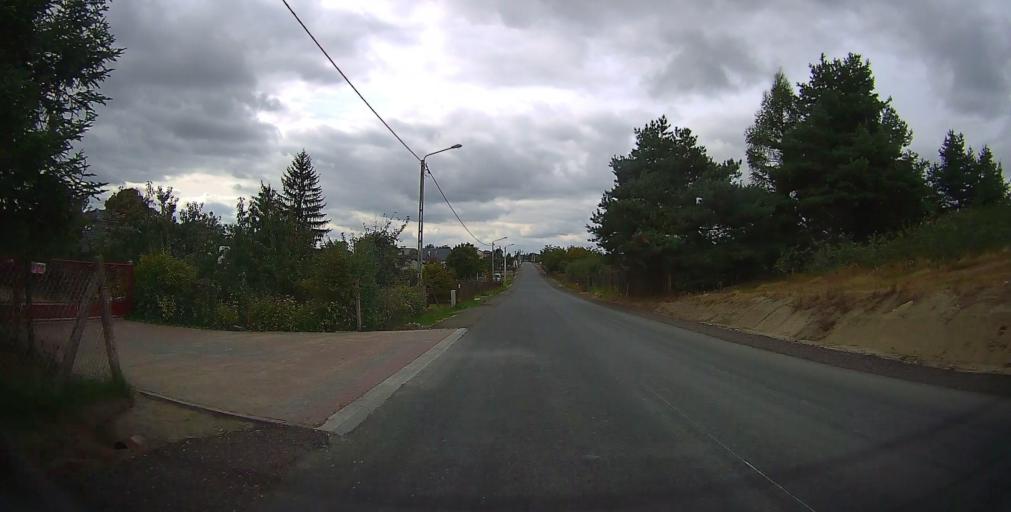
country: PL
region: Masovian Voivodeship
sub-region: Powiat grojecki
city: Belsk Duzy
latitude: 51.8080
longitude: 20.8457
